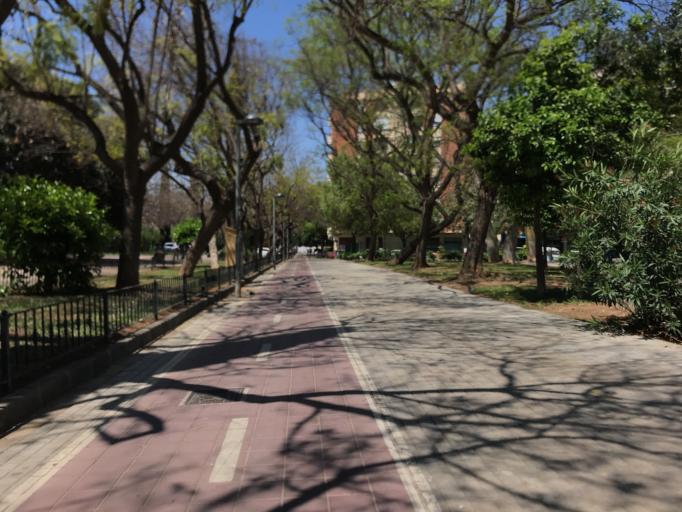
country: ES
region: Valencia
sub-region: Provincia de Valencia
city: Mislata
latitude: 39.4606
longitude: -0.4035
